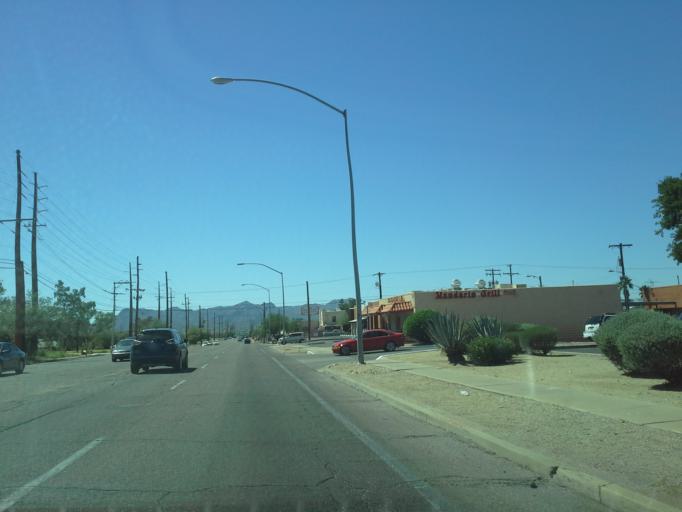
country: US
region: Arizona
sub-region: Pima County
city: Tucson
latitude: 32.2505
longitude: -110.9623
